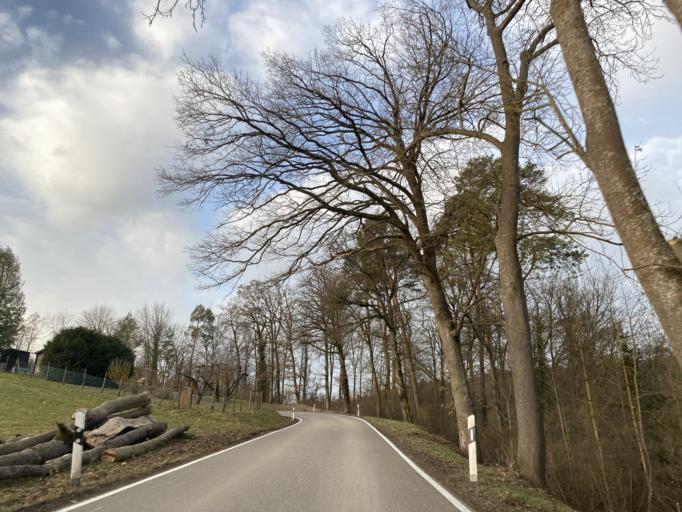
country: DE
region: Baden-Wuerttemberg
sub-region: Karlsruhe Region
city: Wiernsheim
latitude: 48.9091
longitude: 8.8887
